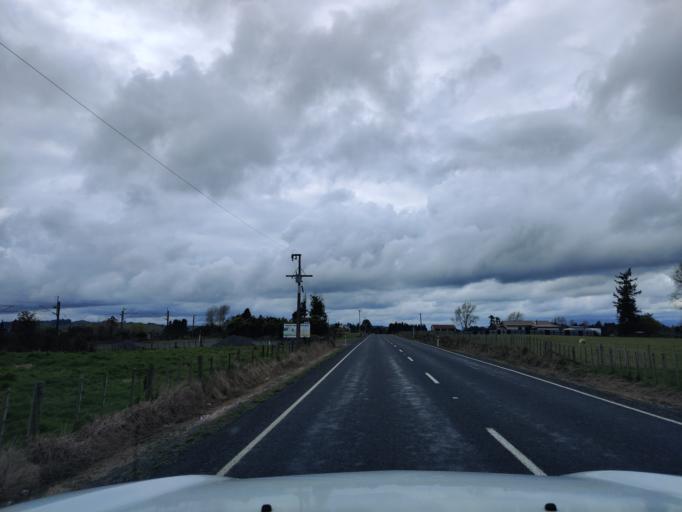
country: NZ
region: Waikato
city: Turangi
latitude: -39.0083
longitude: 175.3774
